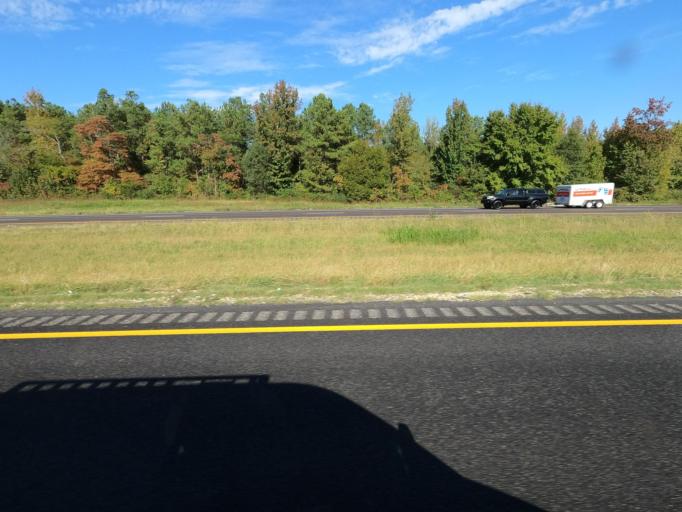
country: US
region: Tennessee
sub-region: Tipton County
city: Mason
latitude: 35.3340
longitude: -89.5503
